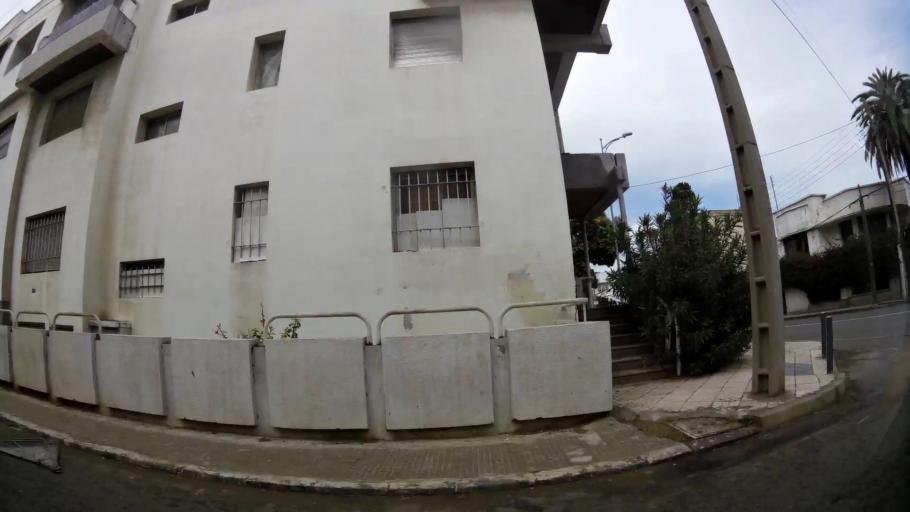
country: MA
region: Grand Casablanca
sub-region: Casablanca
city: Casablanca
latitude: 33.5792
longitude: -7.6098
